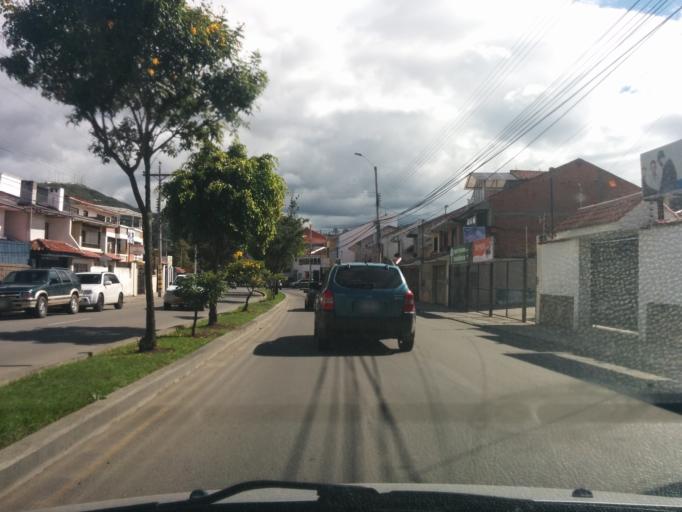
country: EC
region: Azuay
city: Cuenca
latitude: -2.9074
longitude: -78.9936
